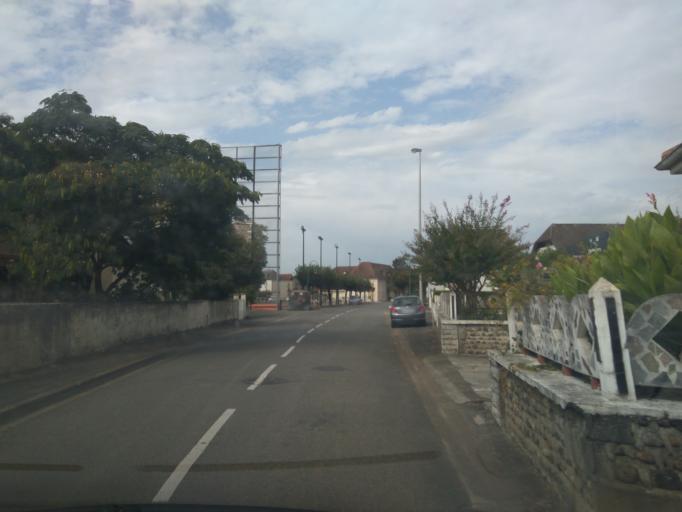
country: FR
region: Aquitaine
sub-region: Departement des Pyrenees-Atlantiques
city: Mourenx
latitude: 43.3650
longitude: -0.5814
